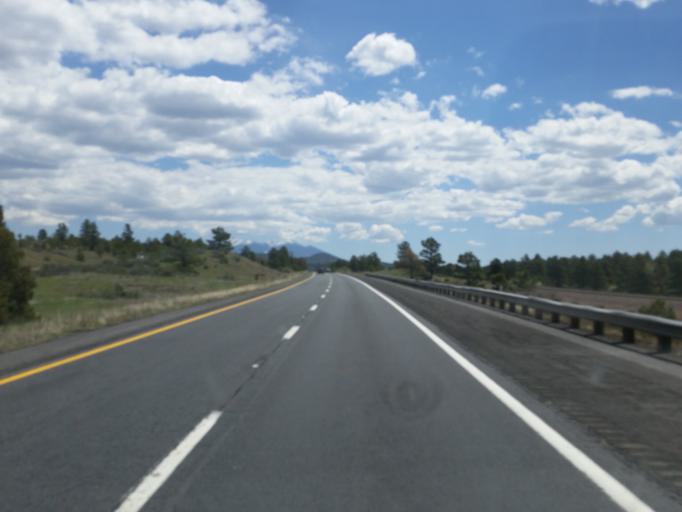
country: US
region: Arizona
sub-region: Coconino County
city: Parks
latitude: 35.2481
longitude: -111.9685
